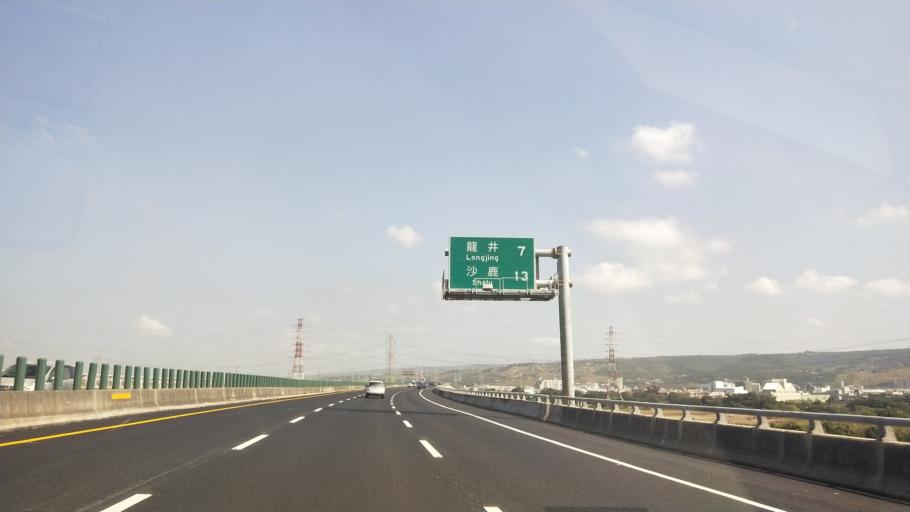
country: TW
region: Taiwan
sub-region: Changhua
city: Chang-hua
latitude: 24.1569
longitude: 120.5234
